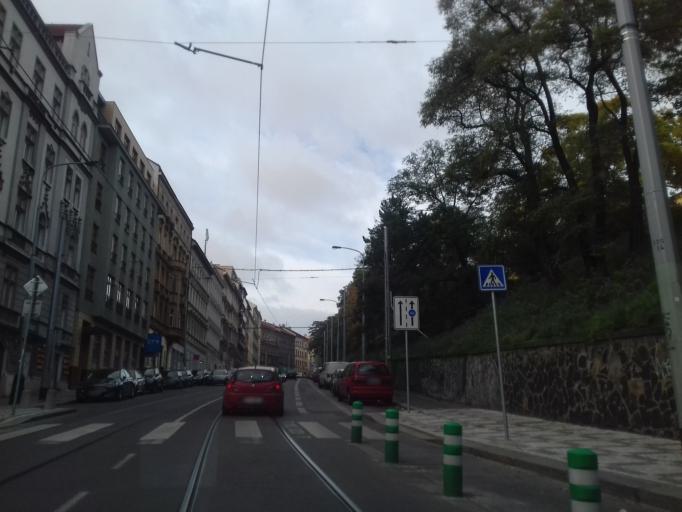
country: CZ
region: Praha
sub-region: Praha 8
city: Karlin
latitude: 50.0720
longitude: 14.4467
